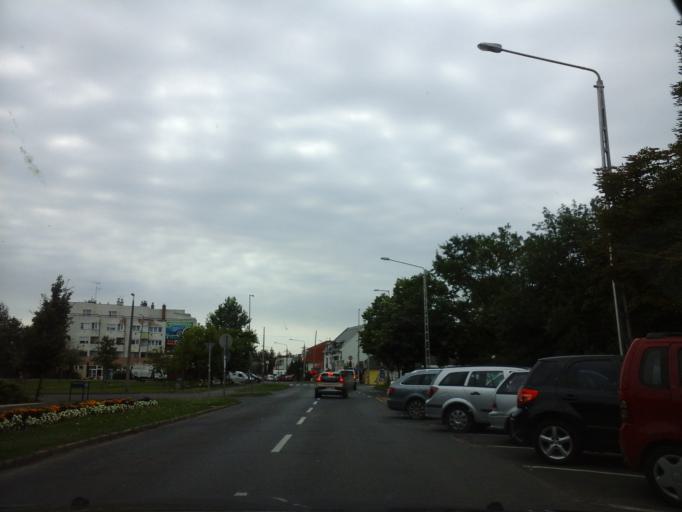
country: HU
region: Hajdu-Bihar
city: Hajduszoboszlo
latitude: 47.4501
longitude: 21.4027
